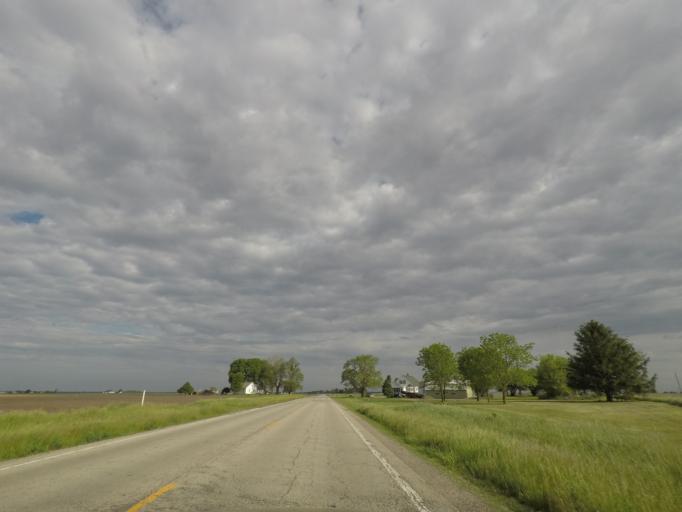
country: US
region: Illinois
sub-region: Logan County
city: Mount Pulaski
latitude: 40.0758
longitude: -89.2964
